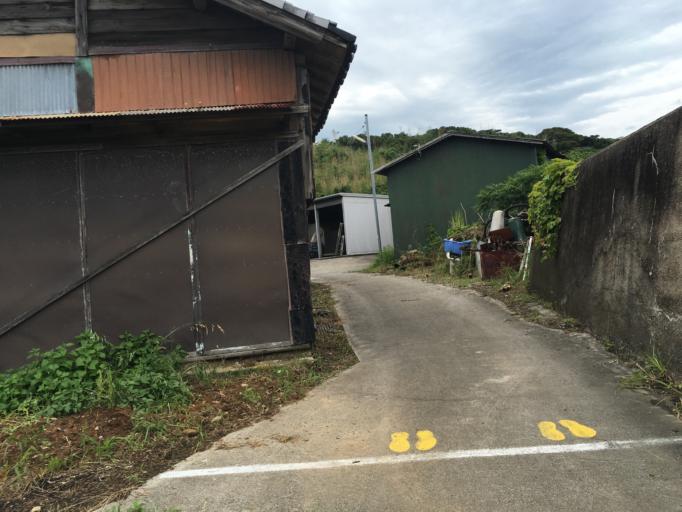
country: JP
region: Aichi
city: Ishiki
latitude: 34.7241
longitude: 137.0496
